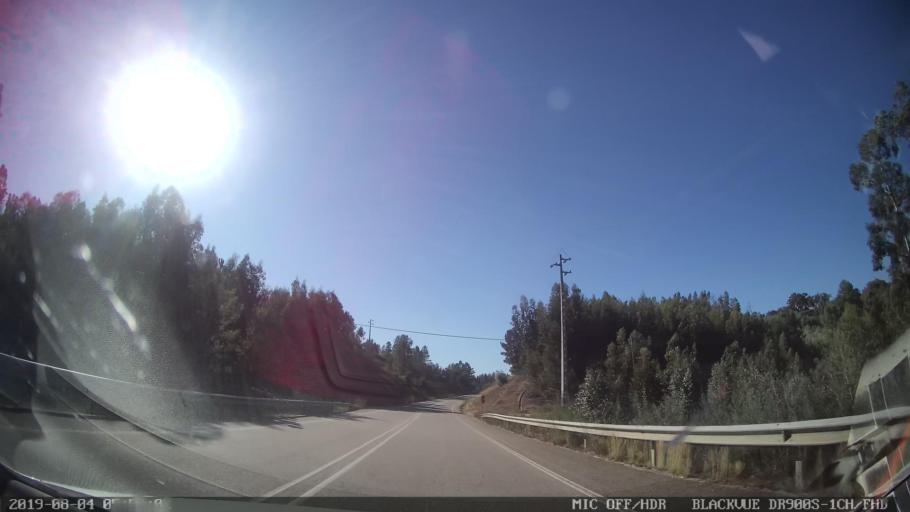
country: PT
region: Portalegre
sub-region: Gaviao
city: Gaviao
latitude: 39.4597
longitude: -7.9388
